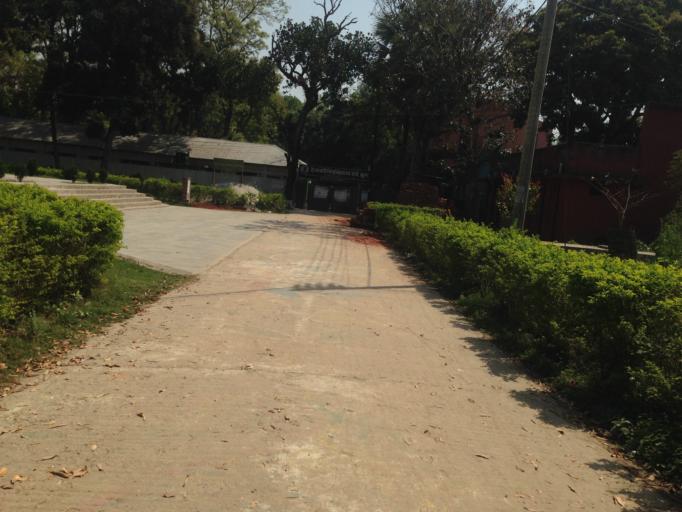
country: BD
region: Dhaka
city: Tangail
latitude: 24.2364
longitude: 89.8906
